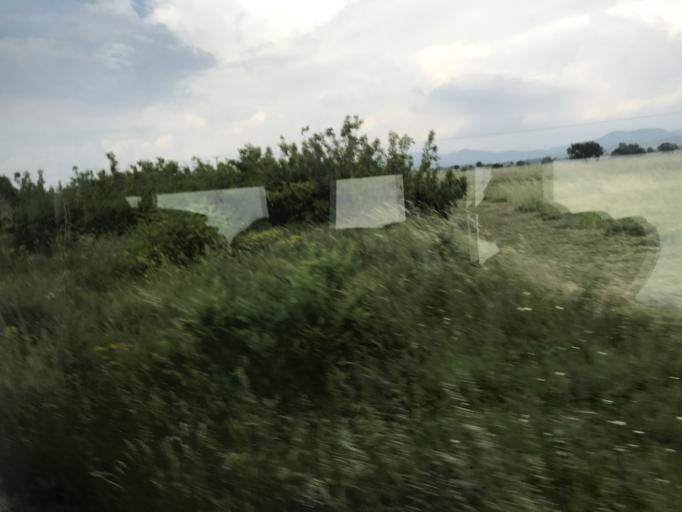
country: GR
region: East Macedonia and Thrace
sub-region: Nomos Rodopis
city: Sapes
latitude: 40.9725
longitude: 25.6436
